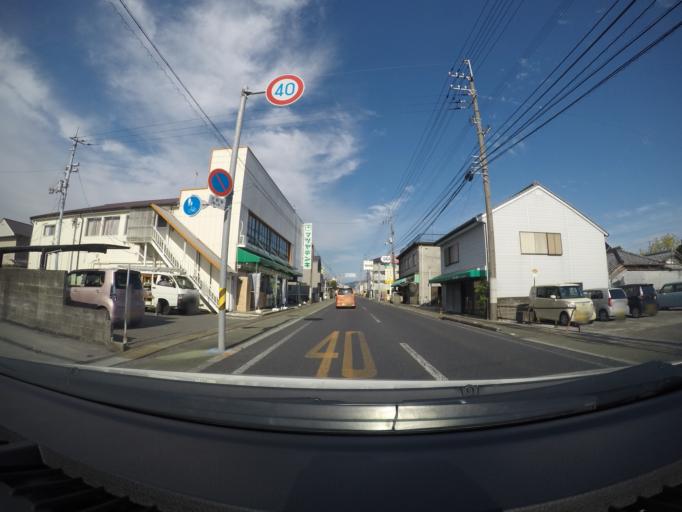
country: JP
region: Kochi
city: Kochi-shi
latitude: 33.6031
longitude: 133.6796
